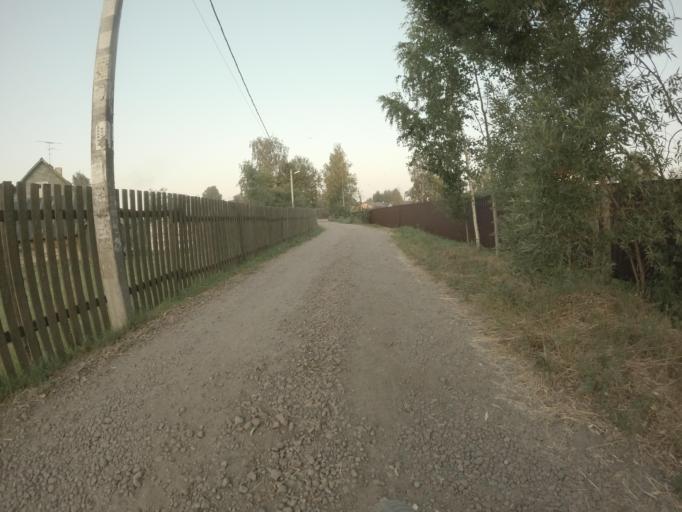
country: RU
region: Leningrad
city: Imeni Sverdlova
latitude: 59.7868
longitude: 30.7177
